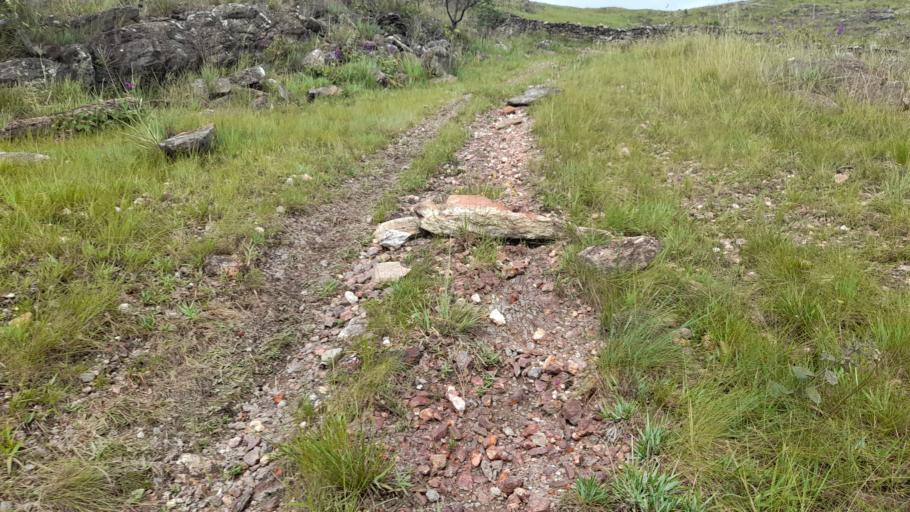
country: BR
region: Minas Gerais
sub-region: Sao Joao Del Rei
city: Sao Joao del Rei
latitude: -21.1174
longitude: -44.2816
